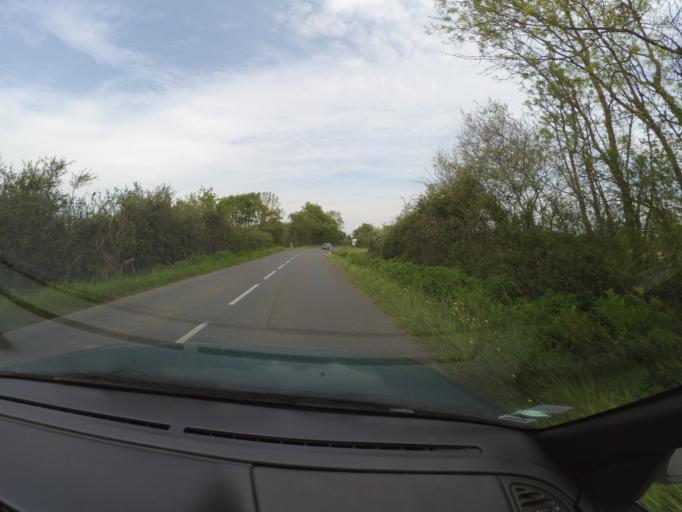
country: FR
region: Pays de la Loire
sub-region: Departement de la Loire-Atlantique
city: Saint-Hilaire-de-Clisson
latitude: 47.0745
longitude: -1.2965
